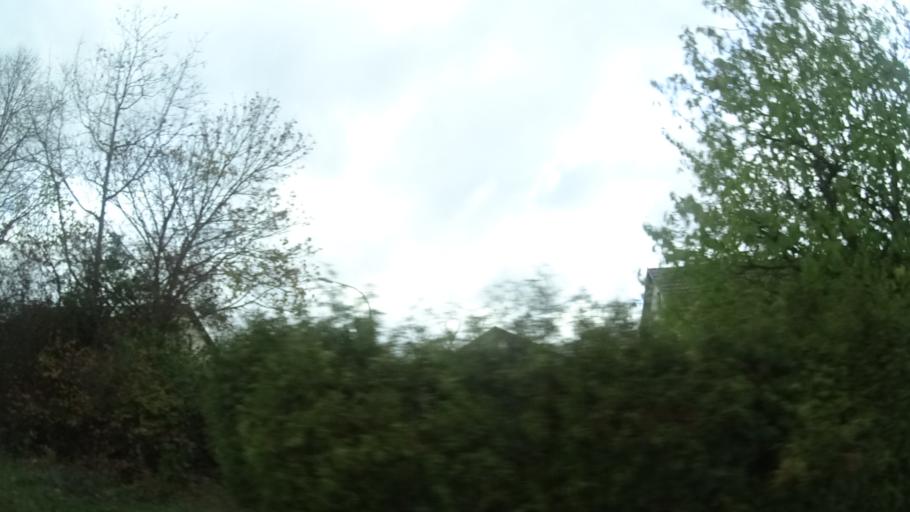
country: DE
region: Bavaria
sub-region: Regierungsbezirk Unterfranken
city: Rodelmaier
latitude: 50.3225
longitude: 10.3014
